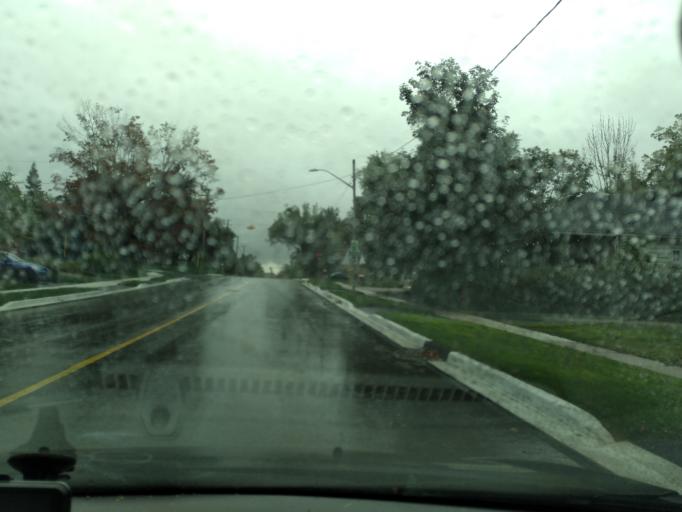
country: CA
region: Ontario
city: Barrie
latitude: 44.4001
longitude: -79.6756
